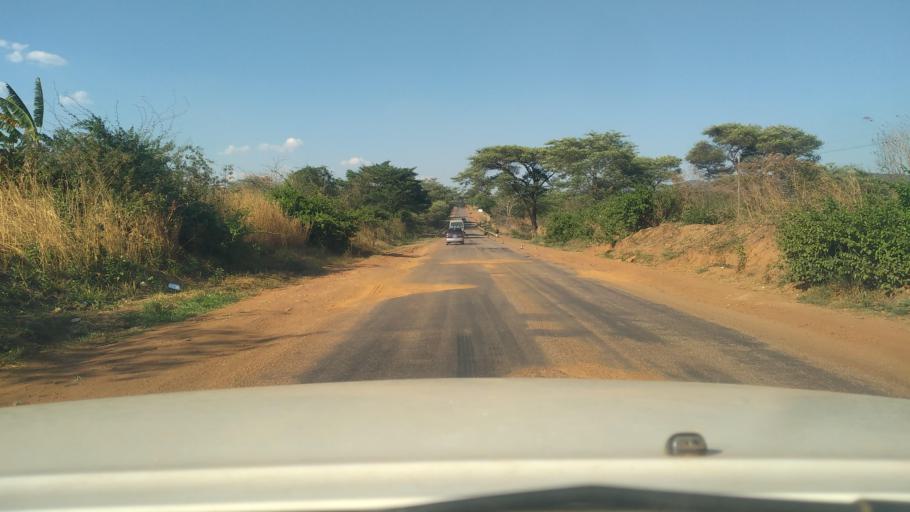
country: ZM
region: Northern
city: Mpika
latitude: -11.7434
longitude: 31.4679
